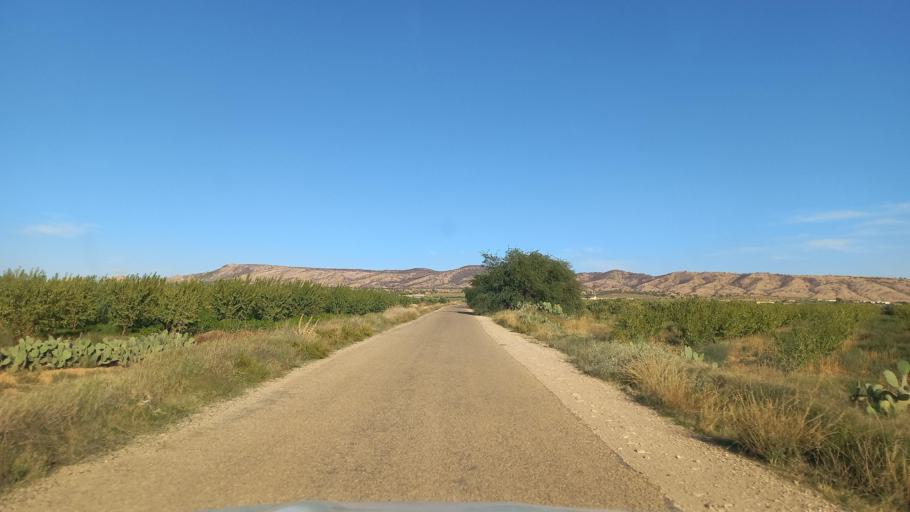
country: TN
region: Al Qasrayn
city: Sbiba
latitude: 35.3369
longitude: 9.1125
